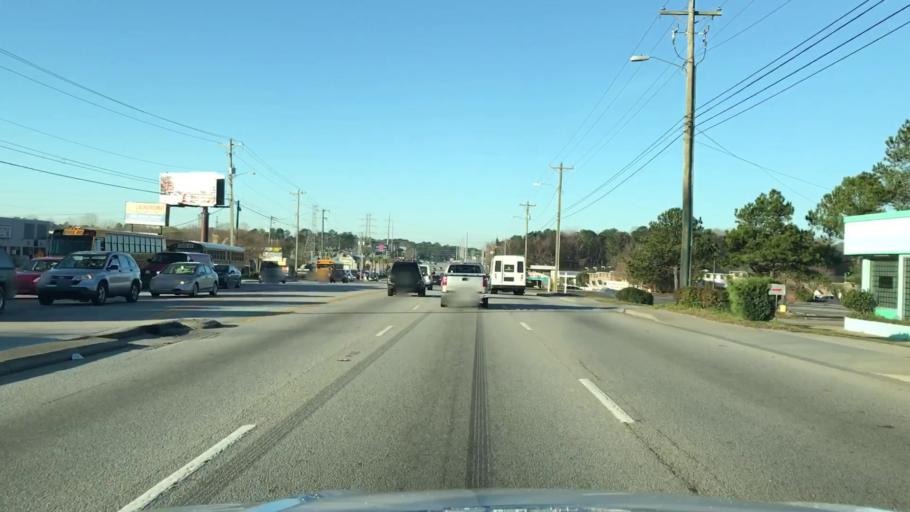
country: US
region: South Carolina
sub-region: Berkeley County
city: Hanahan
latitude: 32.9292
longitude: -80.0734
